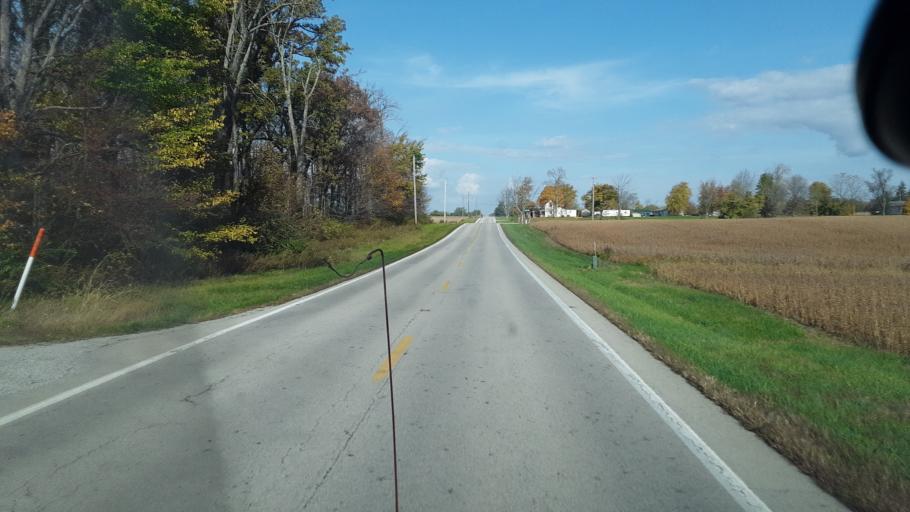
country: US
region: Ohio
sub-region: Clinton County
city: Sabina
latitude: 39.5168
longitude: -83.6928
